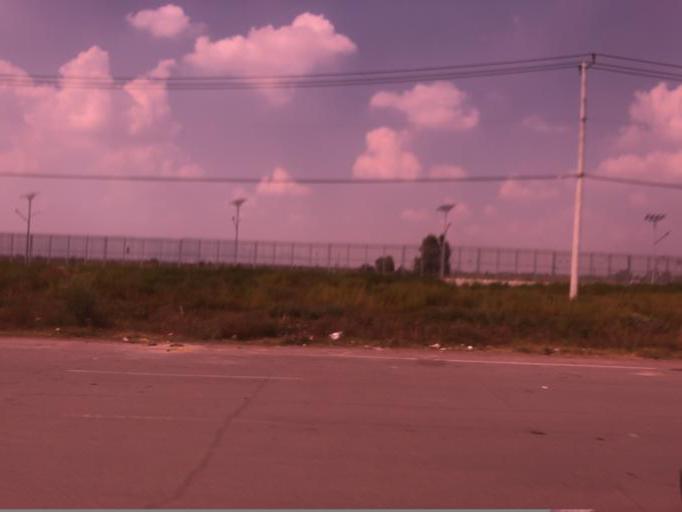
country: MX
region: Mexico
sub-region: Ciudad Nezahualcoyotl
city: Colonia Gustavo Baz Prada
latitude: 19.4715
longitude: -98.9988
